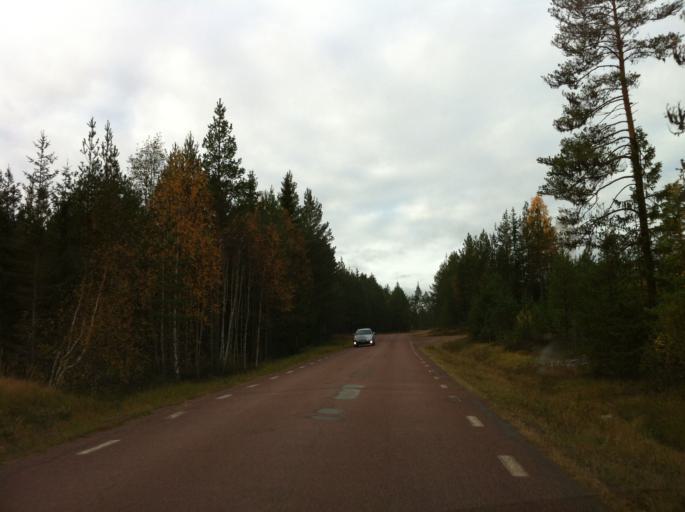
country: SE
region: Dalarna
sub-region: Mora Kommun
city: Mora
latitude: 61.0941
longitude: 14.4406
